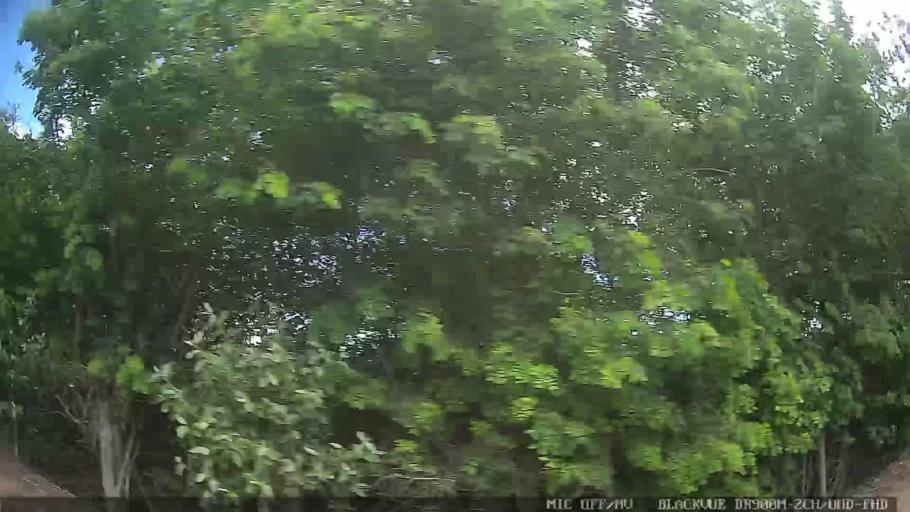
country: BR
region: Sao Paulo
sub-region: Conchas
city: Conchas
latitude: -22.9868
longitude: -47.9923
